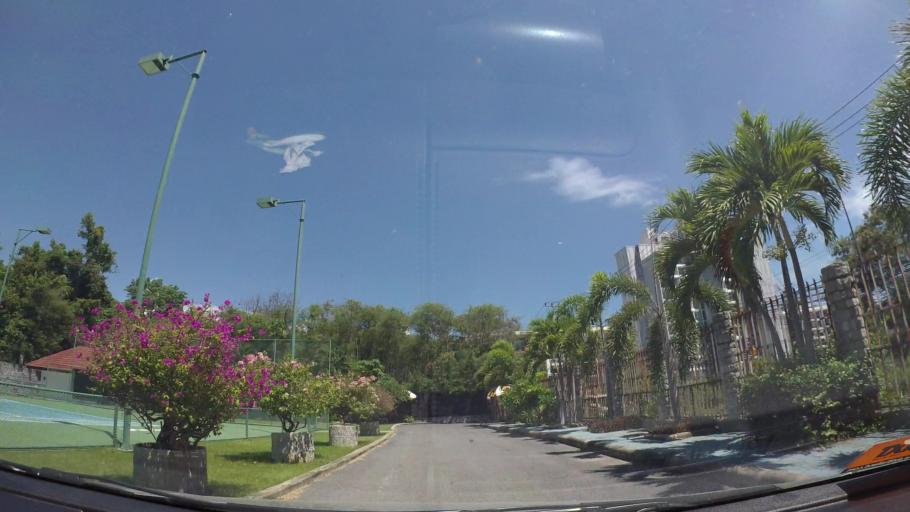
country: TH
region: Chon Buri
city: Phatthaya
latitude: 12.9208
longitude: 100.8644
